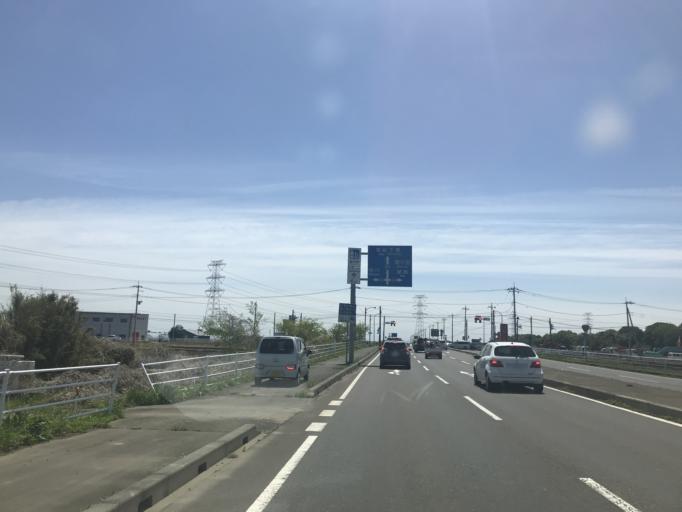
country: JP
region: Ibaraki
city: Shimodate
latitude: 36.2503
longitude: 139.9832
